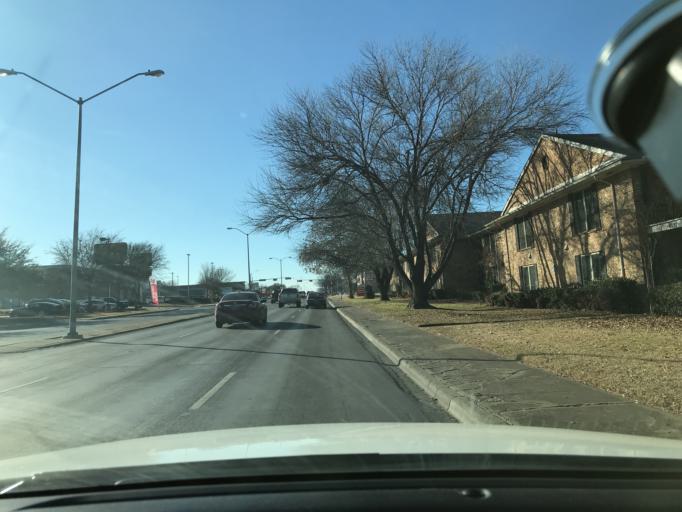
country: US
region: Texas
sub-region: Dallas County
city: Highland Park
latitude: 32.8366
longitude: -96.7592
